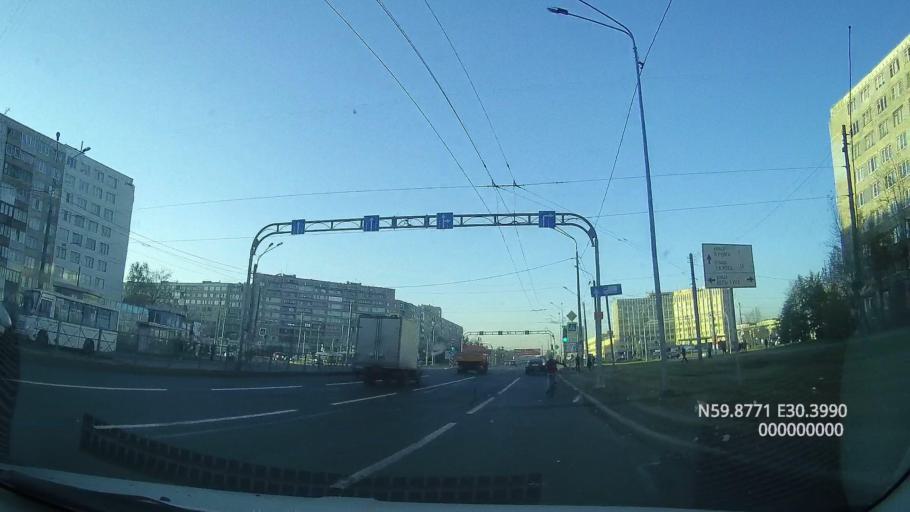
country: RU
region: St.-Petersburg
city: Kupchino
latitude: 59.8767
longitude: 30.3981
